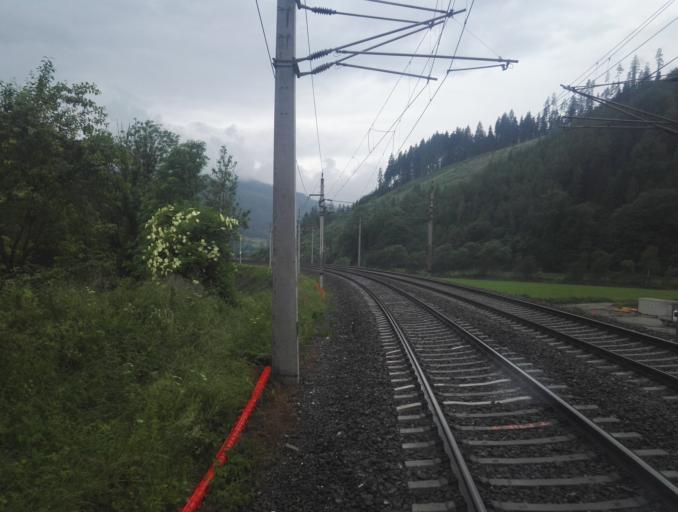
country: AT
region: Styria
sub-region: Politischer Bezirk Bruck-Muerzzuschlag
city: Kindberg
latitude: 47.5237
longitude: 15.4665
